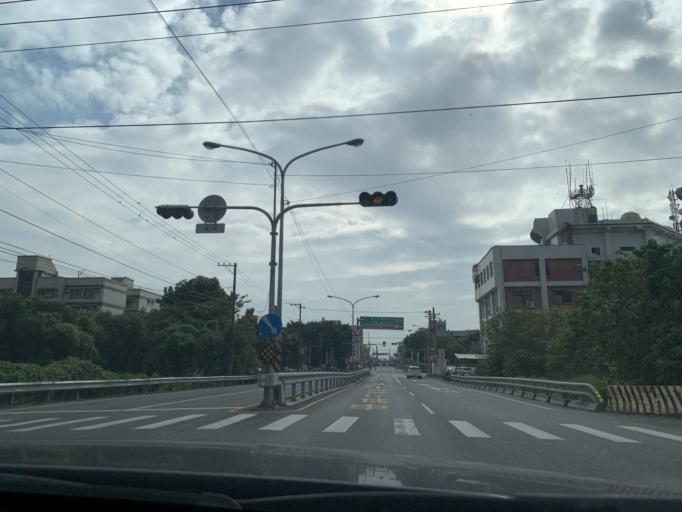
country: TW
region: Taiwan
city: Fengshan
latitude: 22.4639
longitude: 120.4624
